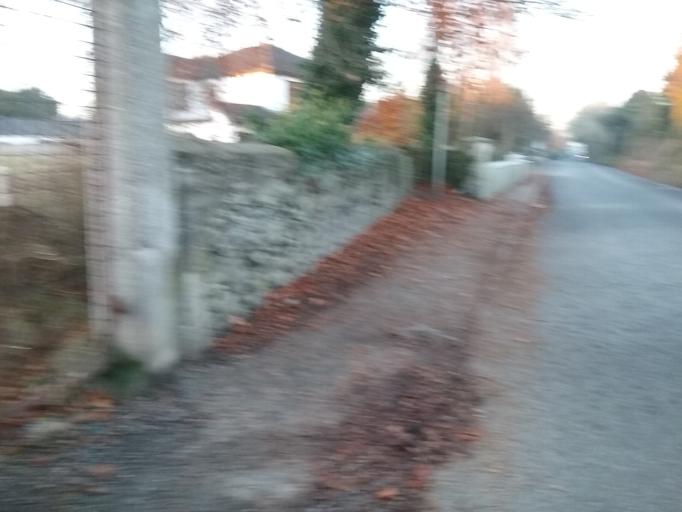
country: IE
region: Leinster
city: Hartstown
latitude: 53.3799
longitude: -6.4055
